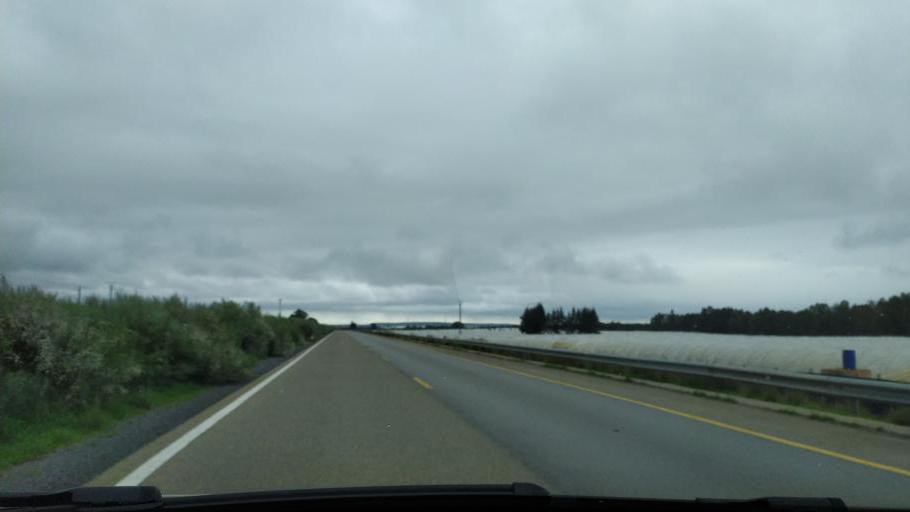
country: MA
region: Gharb-Chrarda-Beni Hssen
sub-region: Kenitra Province
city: Lalla Mimouna
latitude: 34.8972
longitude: -6.2093
